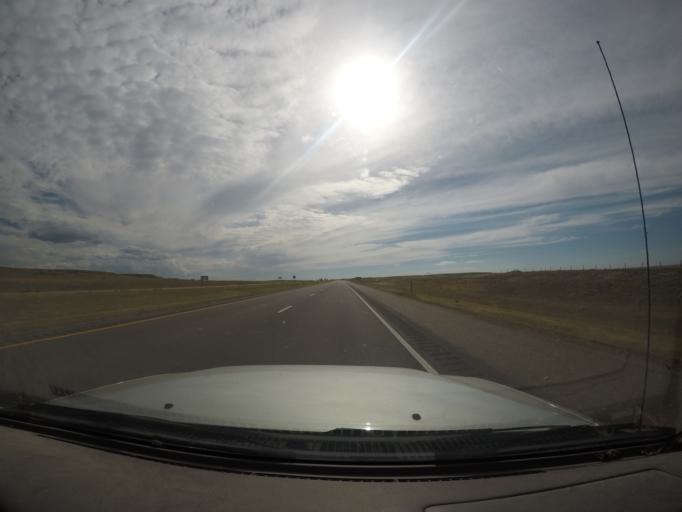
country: US
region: Nebraska
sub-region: Kimball County
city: Kimball
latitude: 41.2150
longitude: -103.6785
